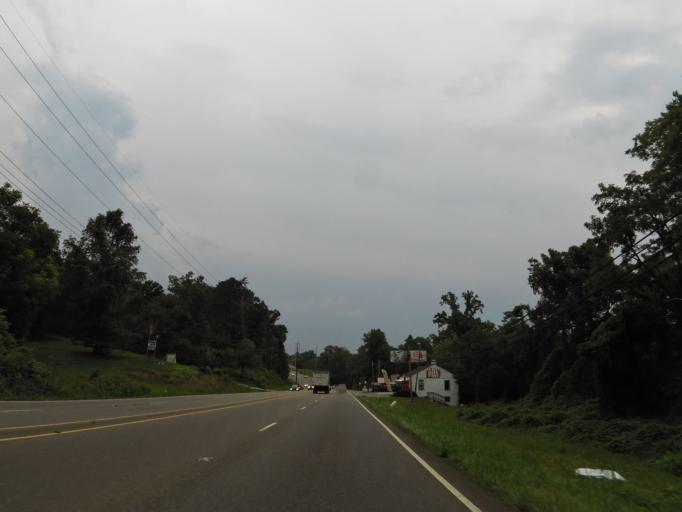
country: US
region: Tennessee
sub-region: Sevier County
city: Seymour
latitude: 35.9036
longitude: -83.8283
